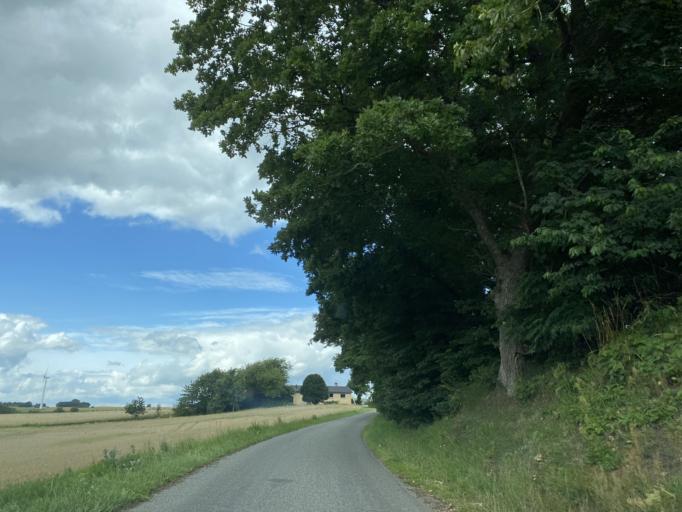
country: DK
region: Central Jutland
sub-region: Silkeborg Kommune
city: Svejbaek
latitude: 56.2368
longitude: 9.6477
